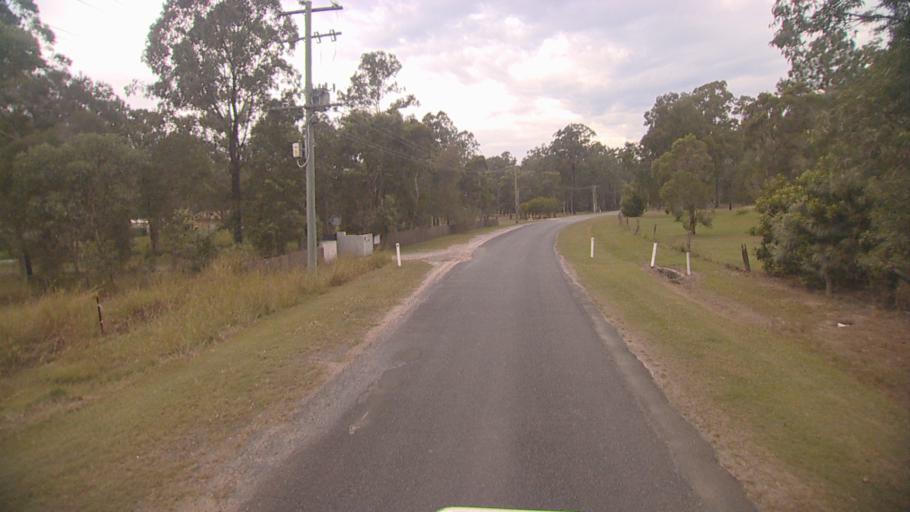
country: AU
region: Queensland
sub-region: Logan
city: Chambers Flat
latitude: -27.7911
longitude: 153.1242
